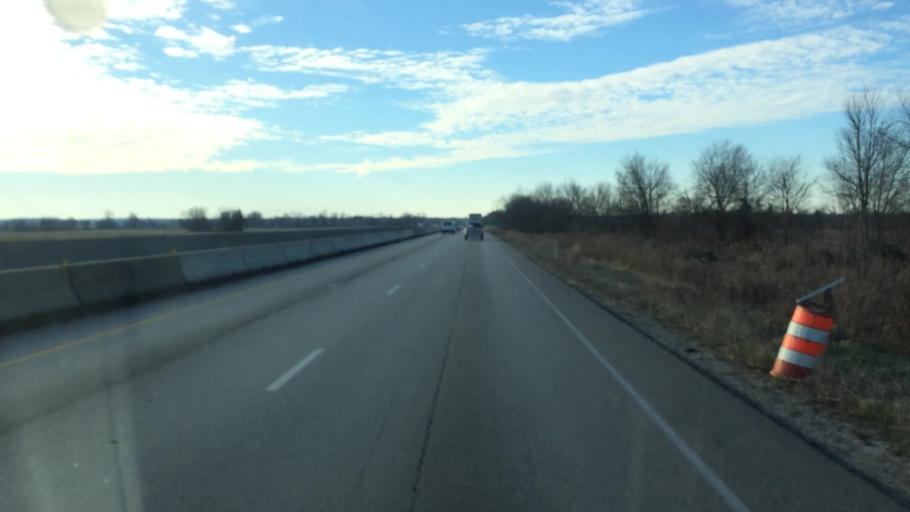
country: US
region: Kentucky
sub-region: Hardin County
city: Elizabethtown
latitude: 37.5855
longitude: -85.8712
